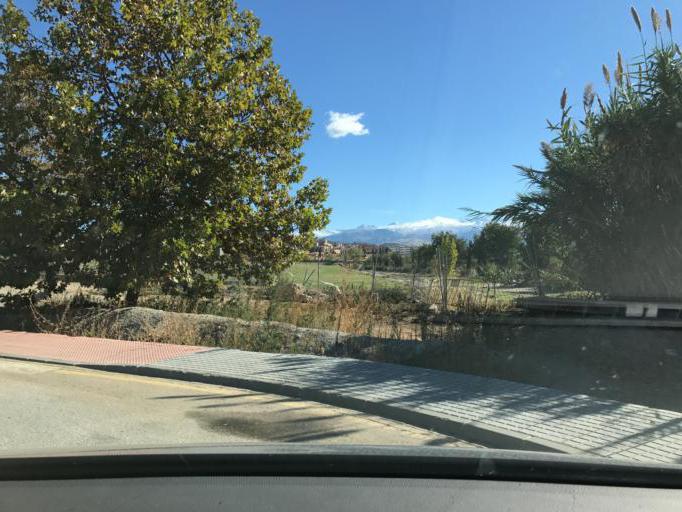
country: ES
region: Andalusia
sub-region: Provincia de Granada
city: Maracena
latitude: 37.2007
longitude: -3.6350
